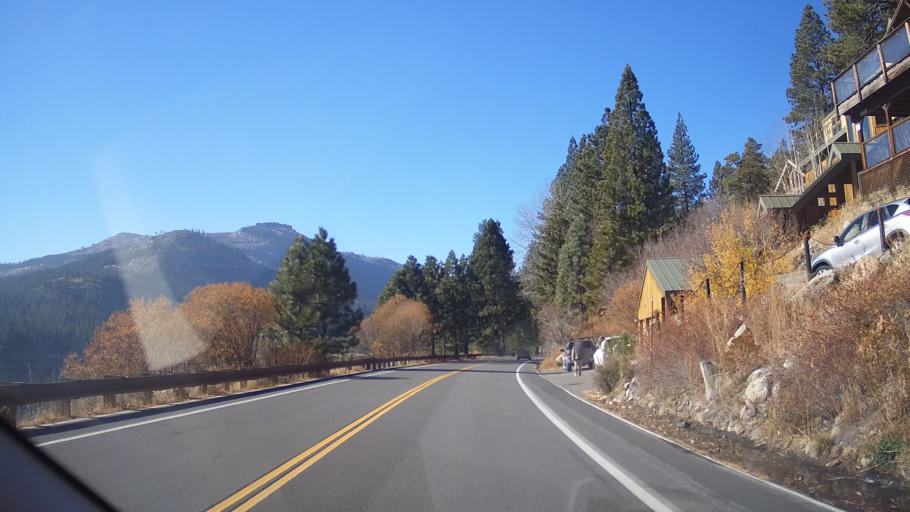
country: US
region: California
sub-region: Nevada County
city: Truckee
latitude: 39.3252
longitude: -120.2722
